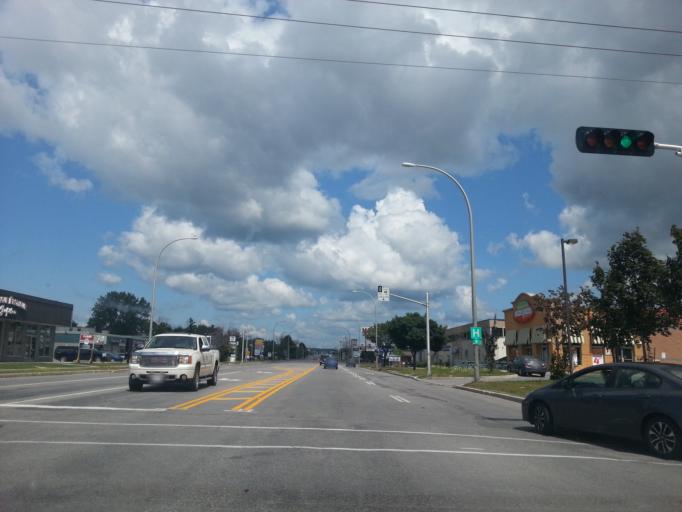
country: CA
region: Quebec
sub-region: Outaouais
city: Gatineau
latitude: 45.4668
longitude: -75.7003
